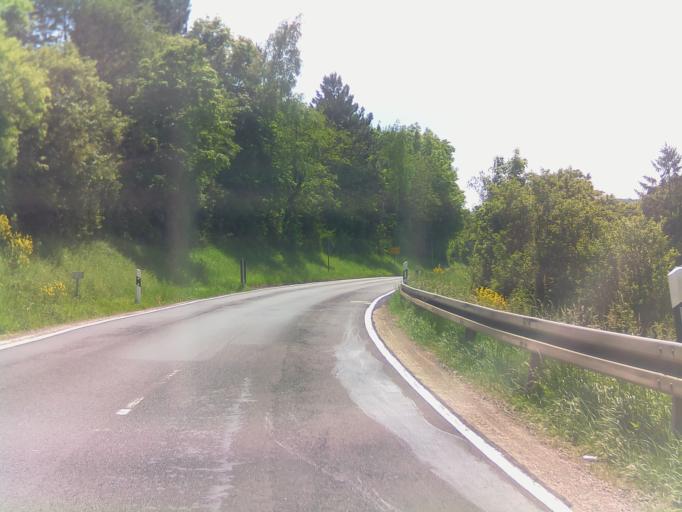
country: DE
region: Bavaria
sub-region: Regierungsbezirk Unterfranken
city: Arnstein
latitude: 49.9833
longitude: 9.9757
